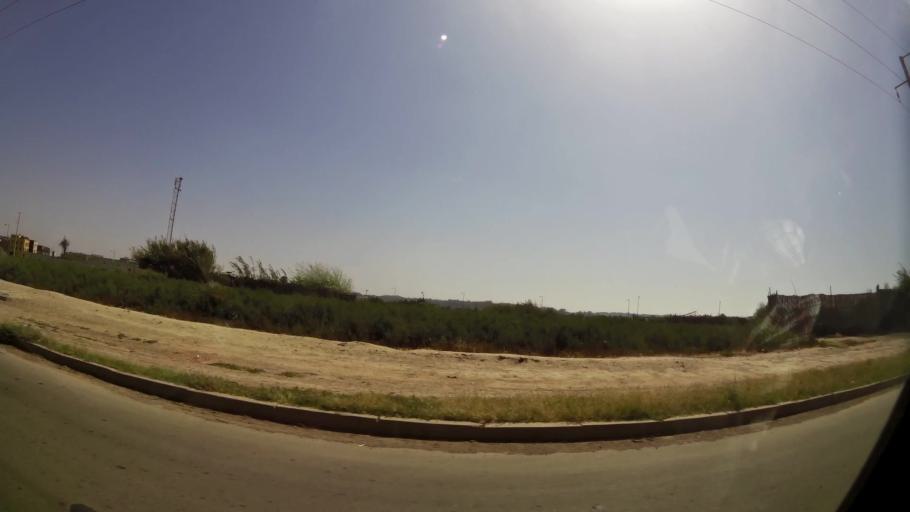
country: MA
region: Souss-Massa-Draa
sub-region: Inezgane-Ait Mellou
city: Inezgane
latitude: 30.3558
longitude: -9.5625
